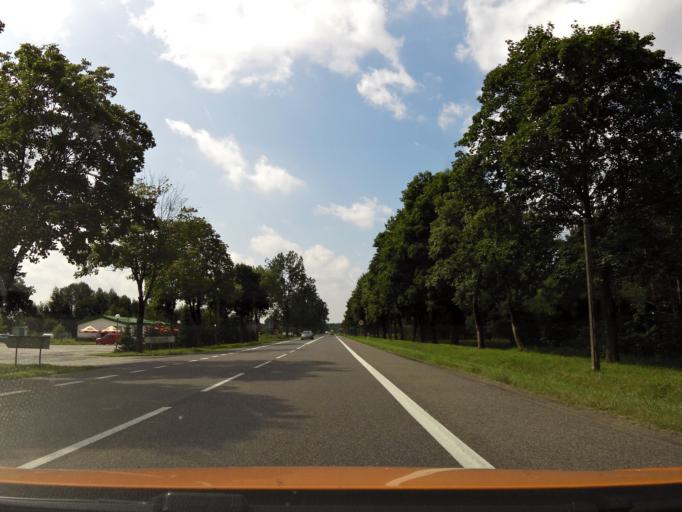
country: PL
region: West Pomeranian Voivodeship
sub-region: Powiat goleniowski
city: Mosty
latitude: 53.6117
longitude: 14.9126
